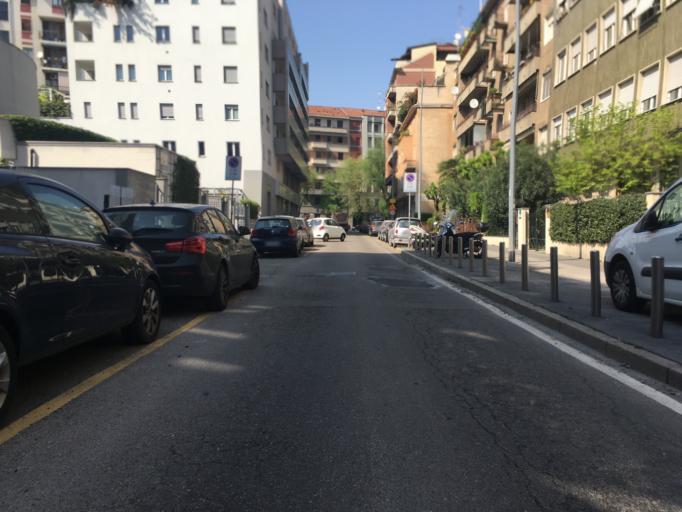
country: IT
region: Lombardy
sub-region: Citta metropolitana di Milano
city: Milano
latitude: 45.4553
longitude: 9.1566
